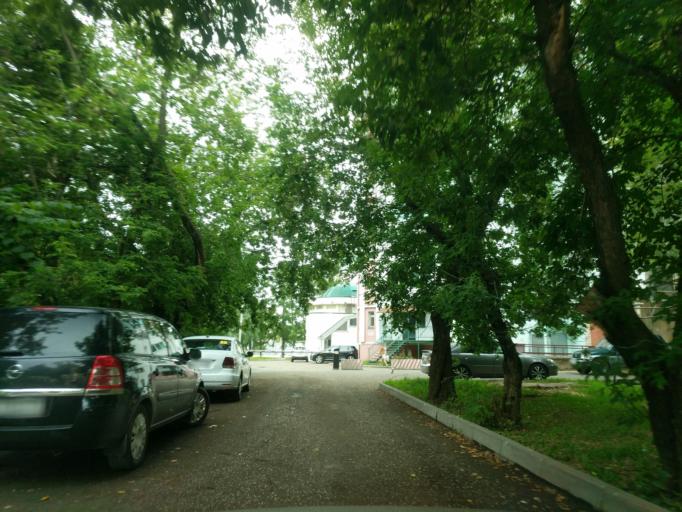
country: RU
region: Kirov
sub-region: Kirovo-Chepetskiy Rayon
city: Kirov
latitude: 58.5951
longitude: 49.6827
